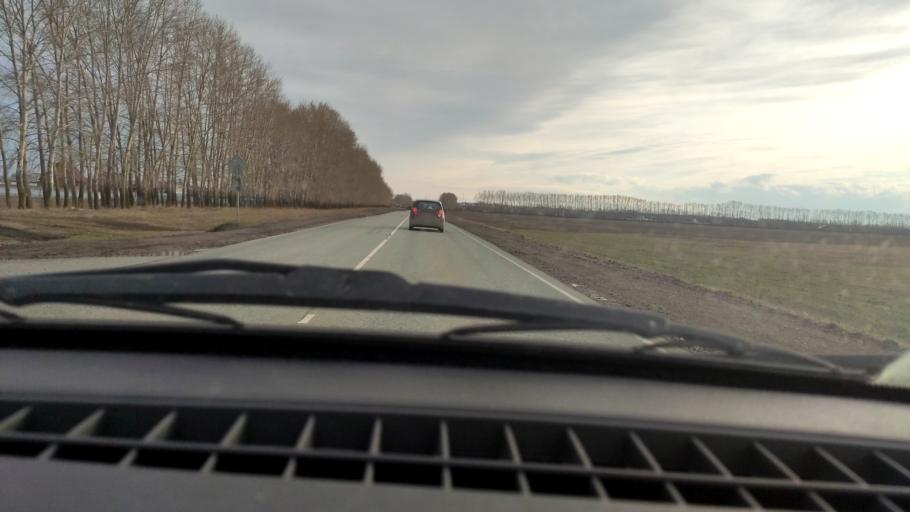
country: RU
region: Bashkortostan
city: Chishmy
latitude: 54.3987
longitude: 55.2105
